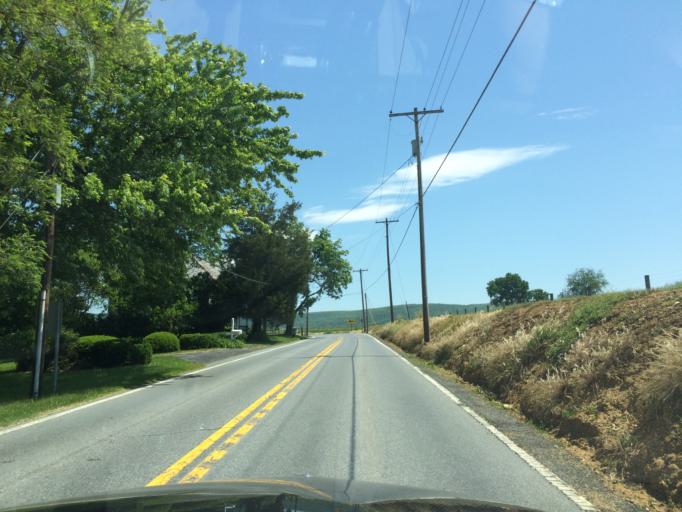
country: US
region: Maryland
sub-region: Frederick County
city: Middletown
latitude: 39.4533
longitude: -77.5384
